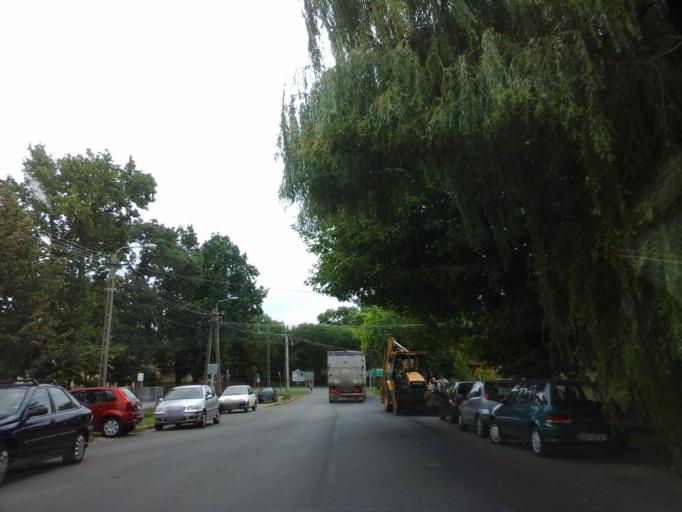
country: HU
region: Hajdu-Bihar
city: Hajduszoboszlo
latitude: 47.4446
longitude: 21.3843
